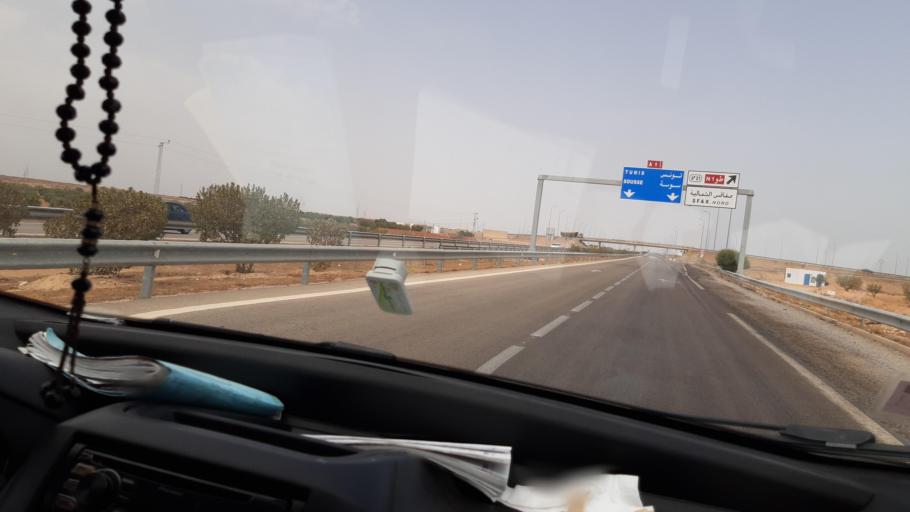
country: TN
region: Safaqis
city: Al Qarmadah
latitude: 34.8888
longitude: 10.7134
